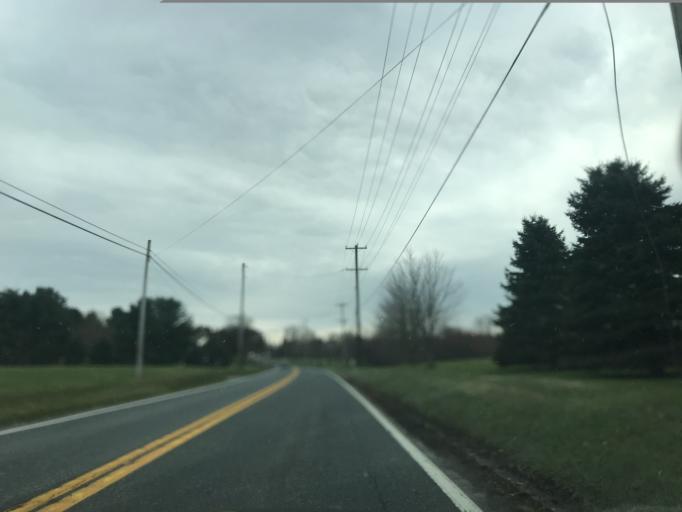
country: US
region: Maryland
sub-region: Harford County
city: Bel Air North
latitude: 39.6461
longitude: -76.3349
